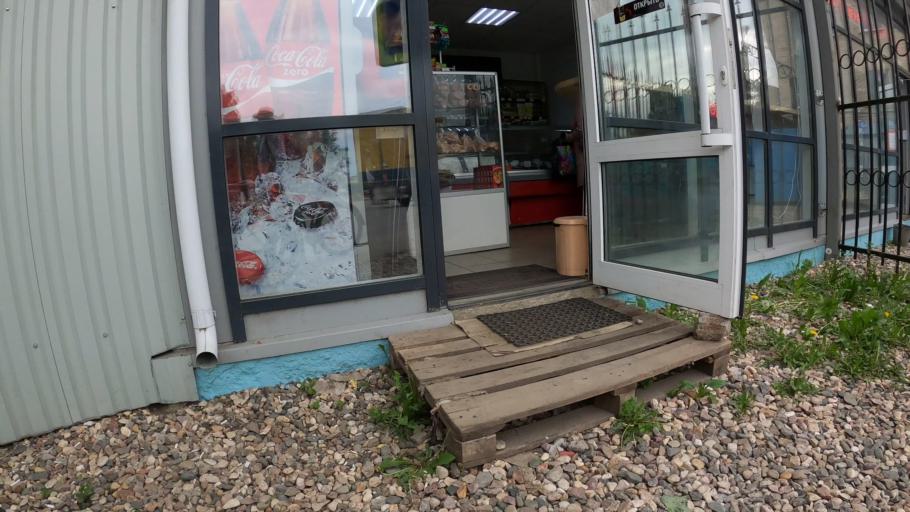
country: RU
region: Moskovskaya
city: Ivanteyevka
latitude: 55.9710
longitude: 37.9258
